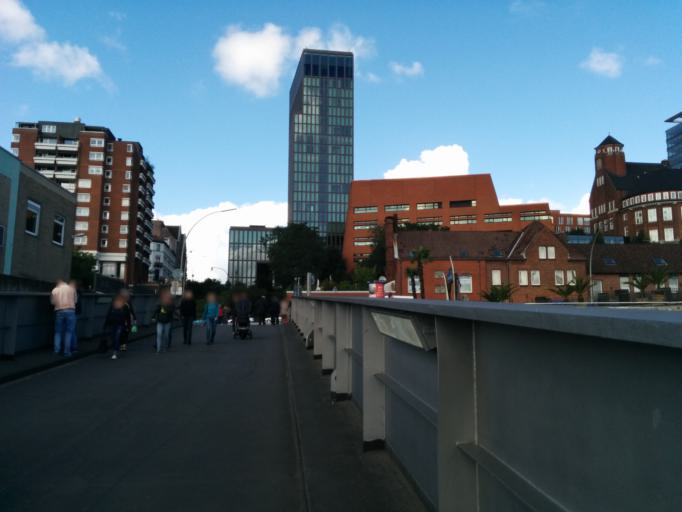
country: DE
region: Hamburg
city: St. Pauli
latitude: 53.5456
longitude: 9.9634
